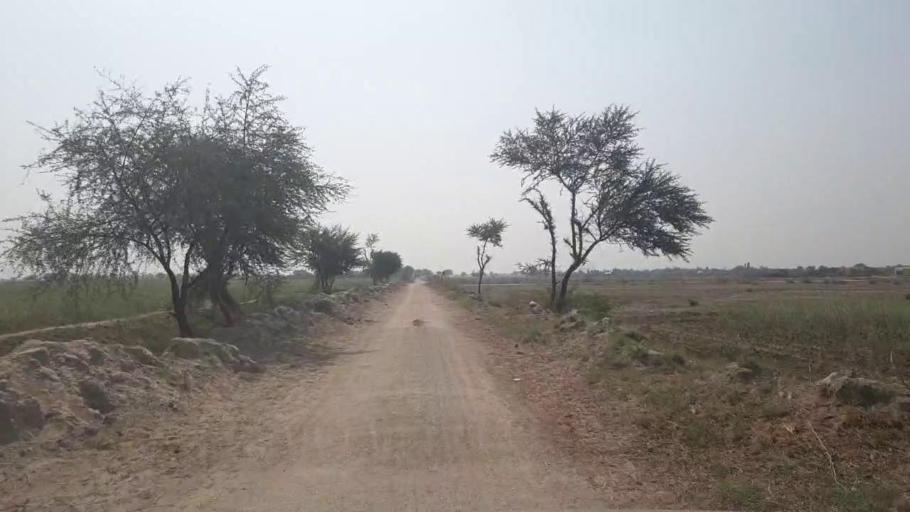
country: PK
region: Sindh
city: Dhoro Naro
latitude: 25.4424
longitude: 69.6259
